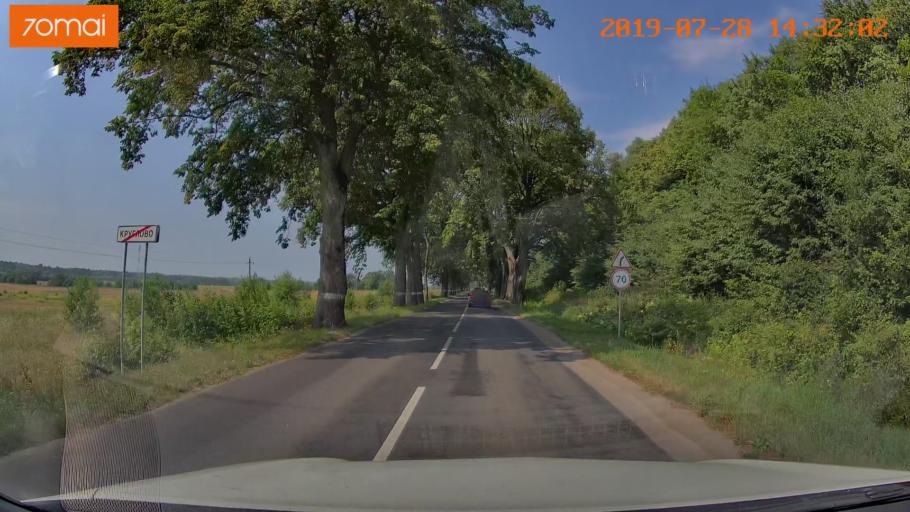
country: RU
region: Kaliningrad
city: Primorsk
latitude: 54.8101
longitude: 20.0457
